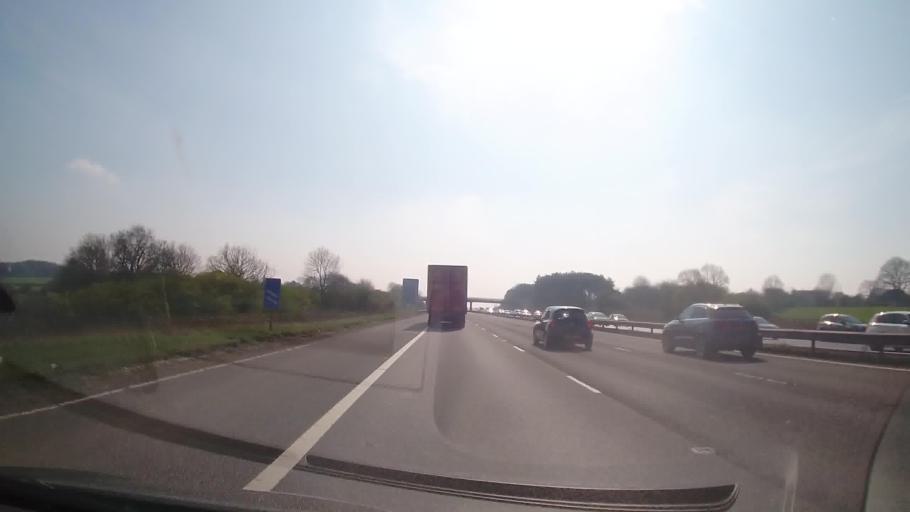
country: GB
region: England
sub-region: Leicestershire
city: Markfield
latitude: 52.7068
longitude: -1.2916
